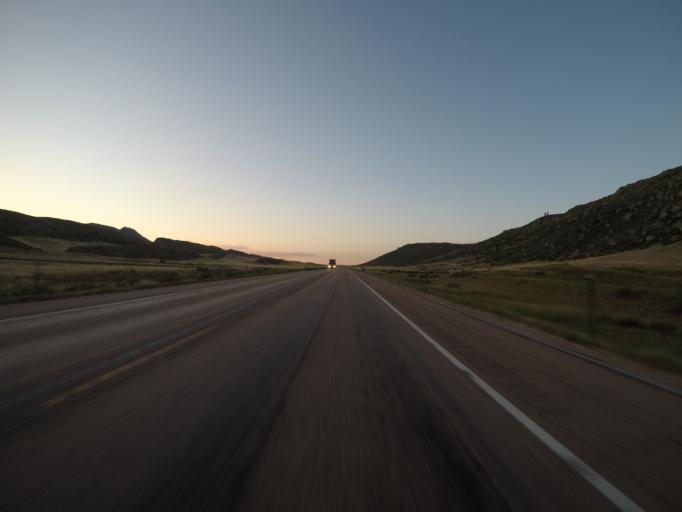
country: US
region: Colorado
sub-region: Larimer County
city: Laporte
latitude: 40.7051
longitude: -105.1734
